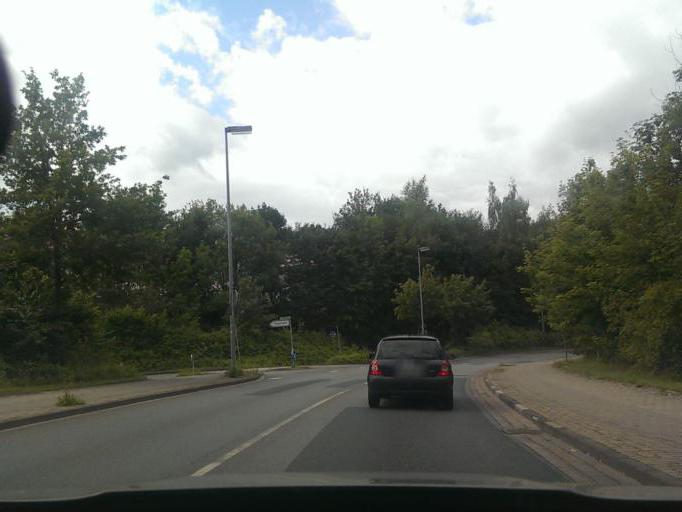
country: DE
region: Lower Saxony
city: Alfeld
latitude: 51.9840
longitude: 9.8305
